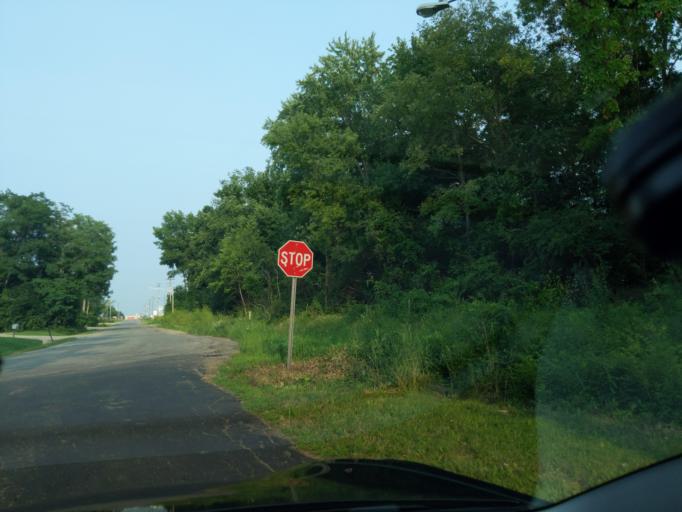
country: US
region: Michigan
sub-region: Jackson County
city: Jackson
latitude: 42.2710
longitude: -84.4608
